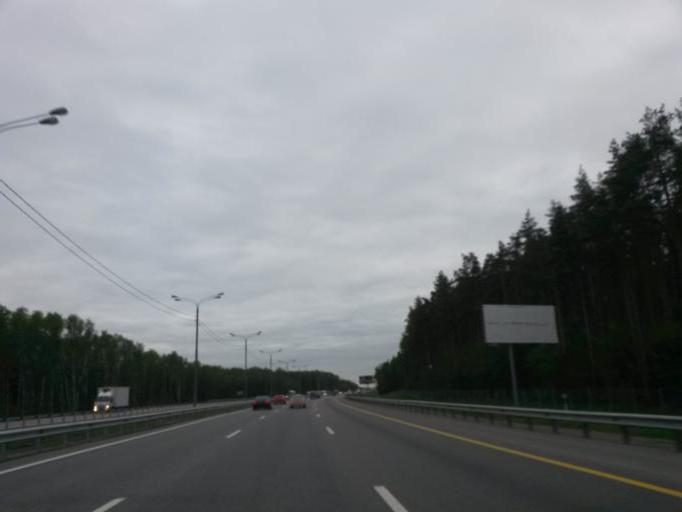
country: RU
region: Moskovskaya
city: Vostryakovo
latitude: 55.4396
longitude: 37.7987
